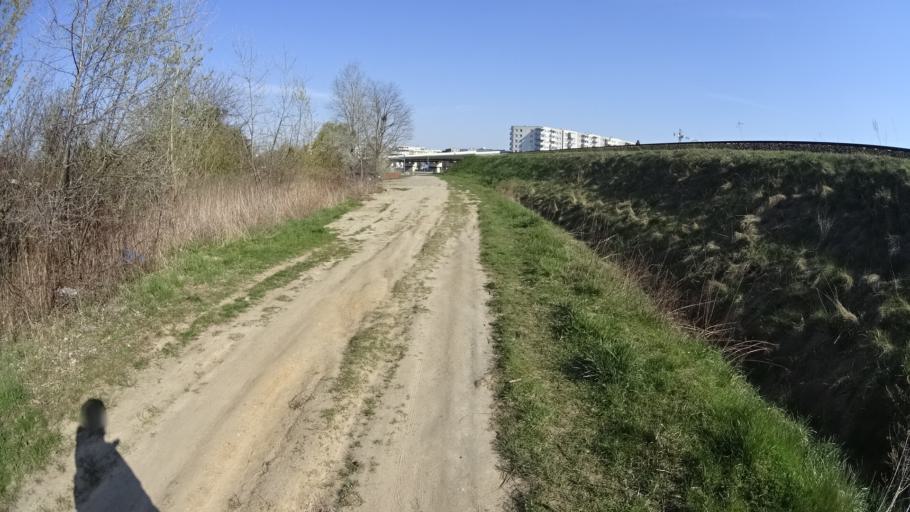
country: PL
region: Masovian Voivodeship
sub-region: Warszawa
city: Bemowo
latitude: 52.2447
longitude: 20.8919
